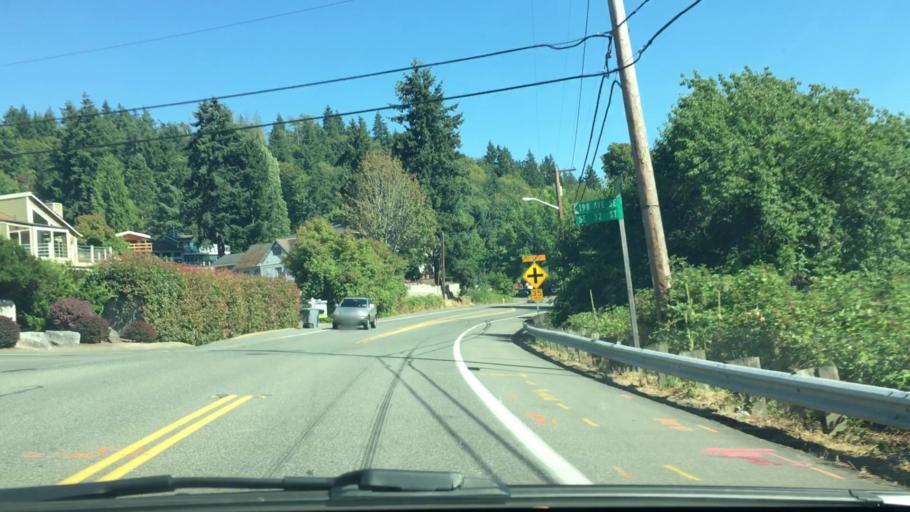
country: US
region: Washington
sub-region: King County
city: West Lake Sammamish
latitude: 47.5810
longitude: -122.0769
